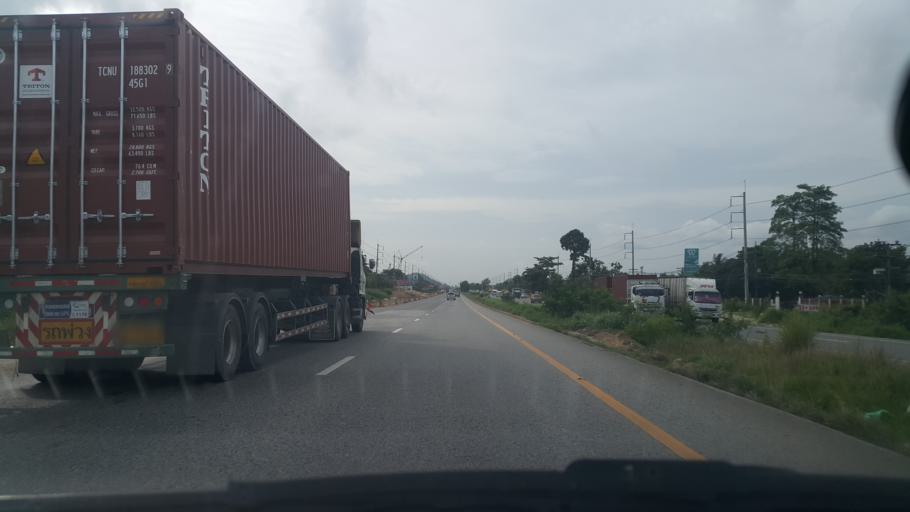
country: TH
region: Rayong
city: Nikhom Phattana
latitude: 12.7981
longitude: 101.1498
